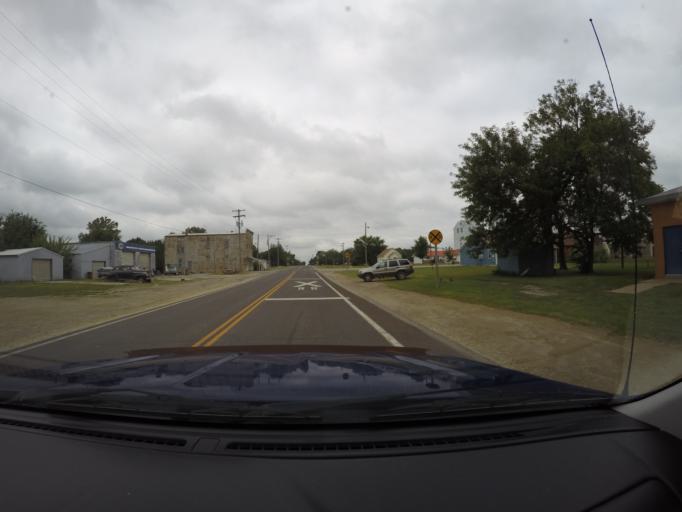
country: US
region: Kansas
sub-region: Morris County
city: Council Grove
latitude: 38.8426
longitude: -96.5940
